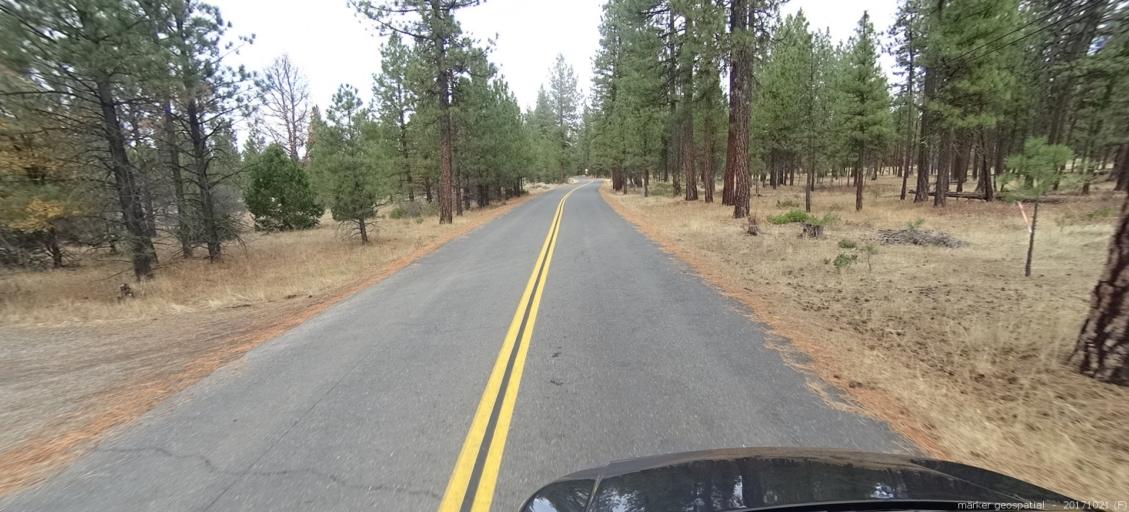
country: US
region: California
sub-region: Shasta County
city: Burney
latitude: 40.9319
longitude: -121.6432
